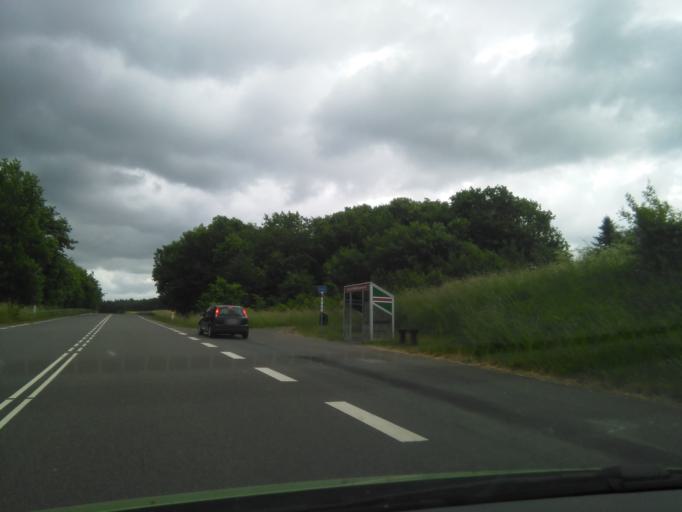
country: DK
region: Capital Region
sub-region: Bornholm Kommune
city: Akirkeby
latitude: 55.2230
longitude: 14.8923
